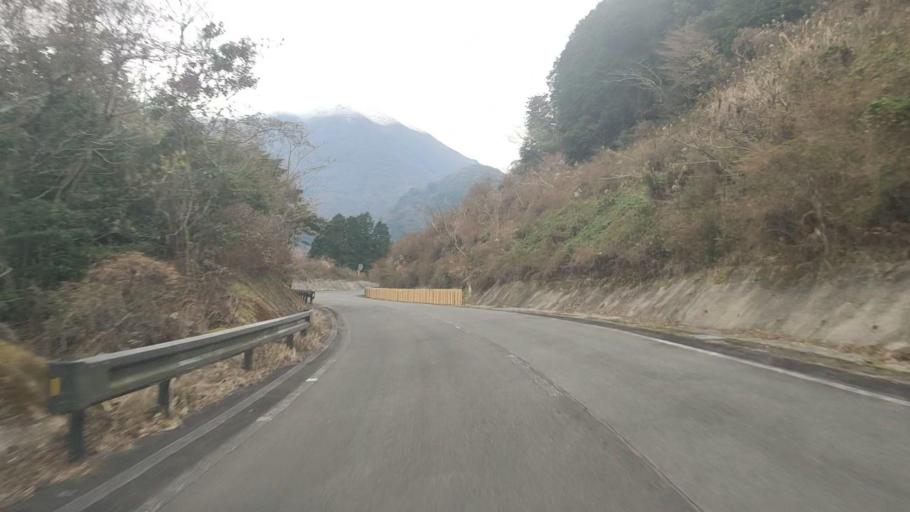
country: JP
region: Nagasaki
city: Shimabara
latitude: 32.7870
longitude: 130.2834
